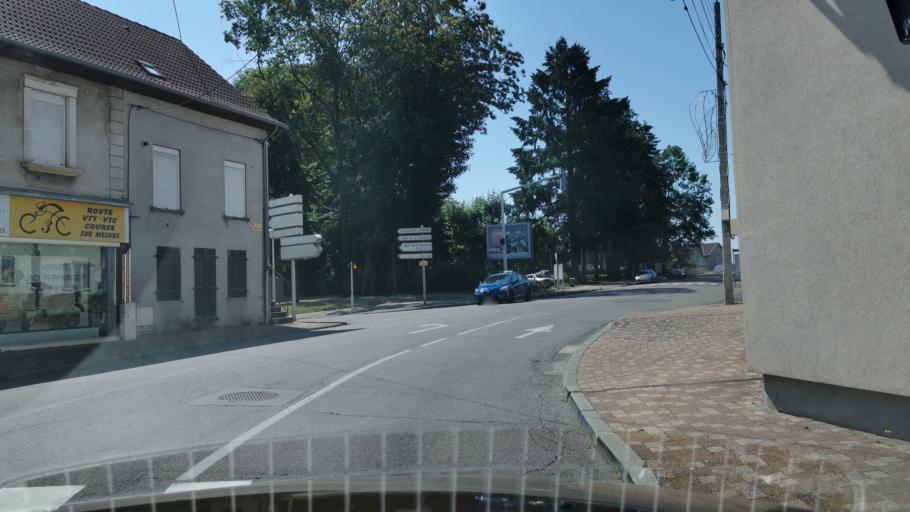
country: FR
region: Bourgogne
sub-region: Departement de Saone-et-Loire
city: Le Creusot
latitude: 46.8034
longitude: 4.4131
